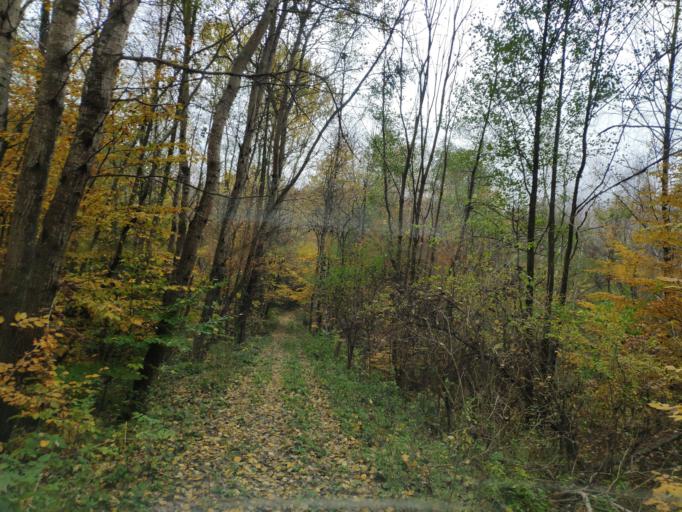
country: SK
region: Kosicky
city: Moldava nad Bodvou
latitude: 48.7286
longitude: 21.0926
